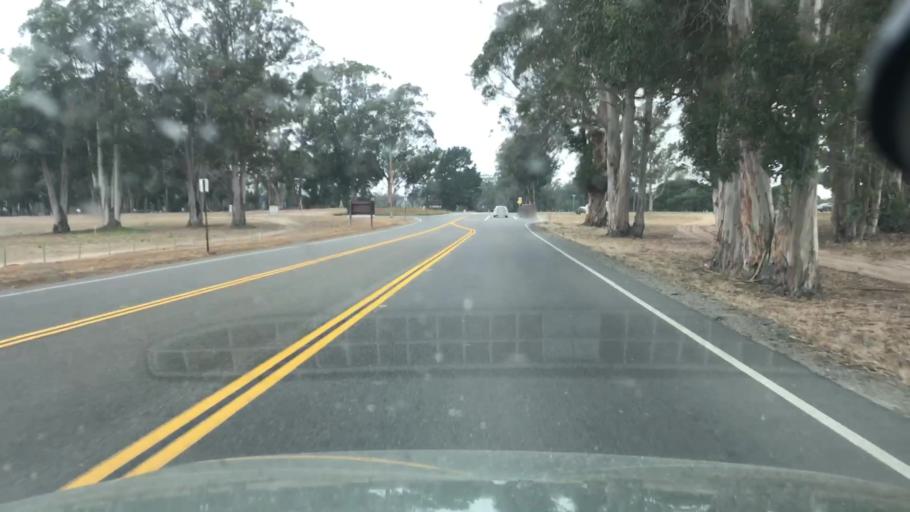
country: US
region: California
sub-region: Santa Barbara County
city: Vandenberg Village
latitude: 34.6816
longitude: -120.5000
